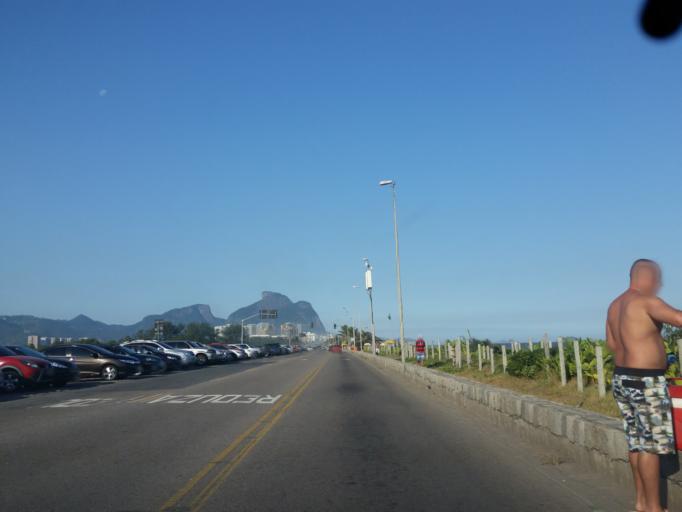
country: BR
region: Rio de Janeiro
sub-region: Nilopolis
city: Nilopolis
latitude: -23.0126
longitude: -43.3881
